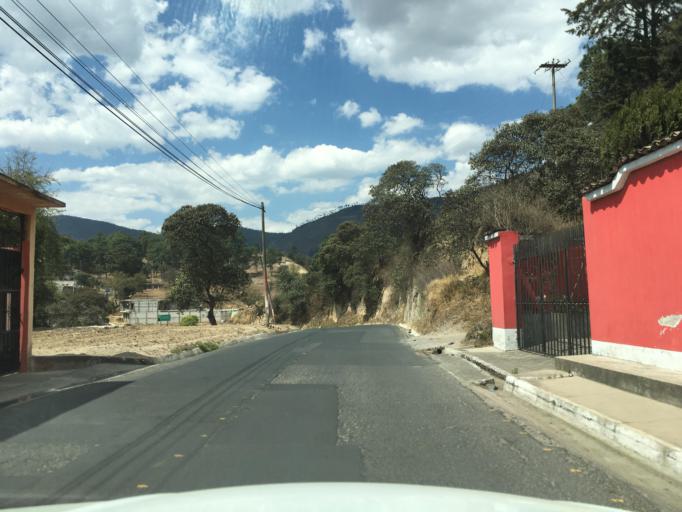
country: GT
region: Quetzaltenango
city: Salcaja
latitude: 14.9054
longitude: -91.4585
